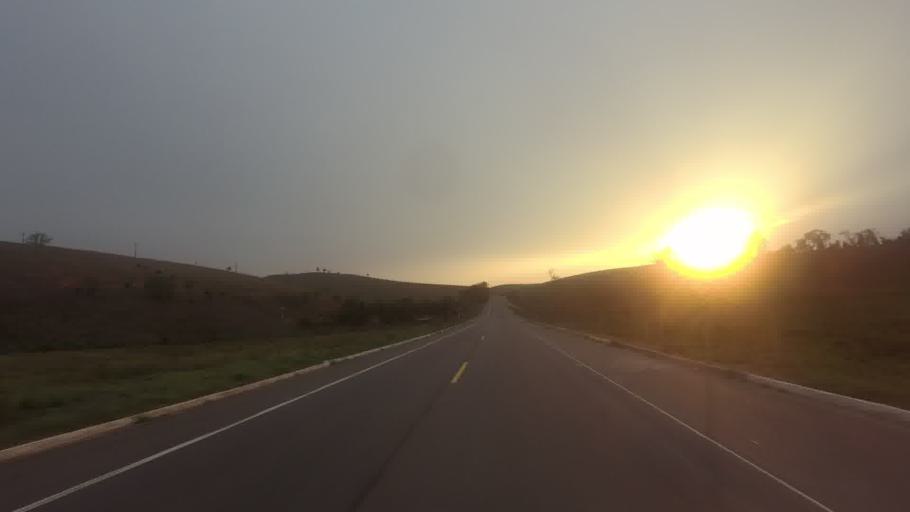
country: BR
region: Minas Gerais
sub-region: Recreio
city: Recreio
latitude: -21.7193
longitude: -42.4344
